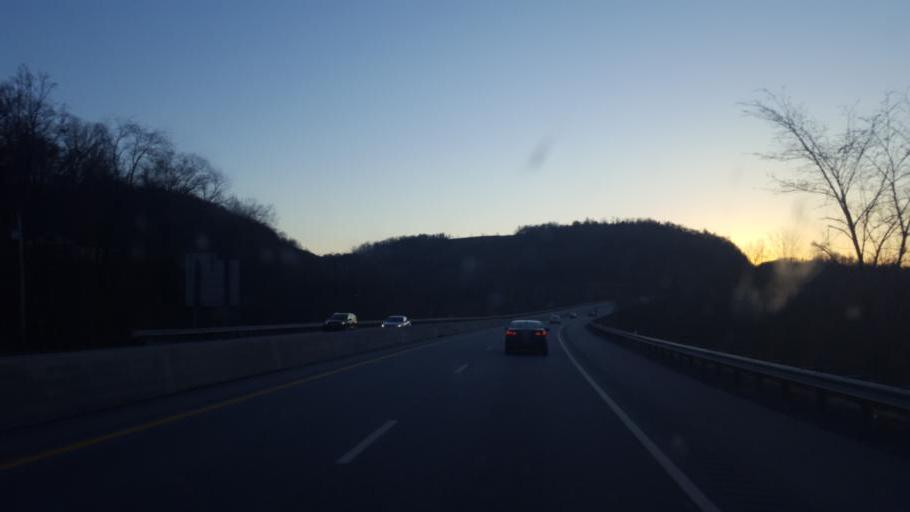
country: US
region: Ohio
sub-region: Belmont County
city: Wolfhurst
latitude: 40.0648
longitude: -80.7698
